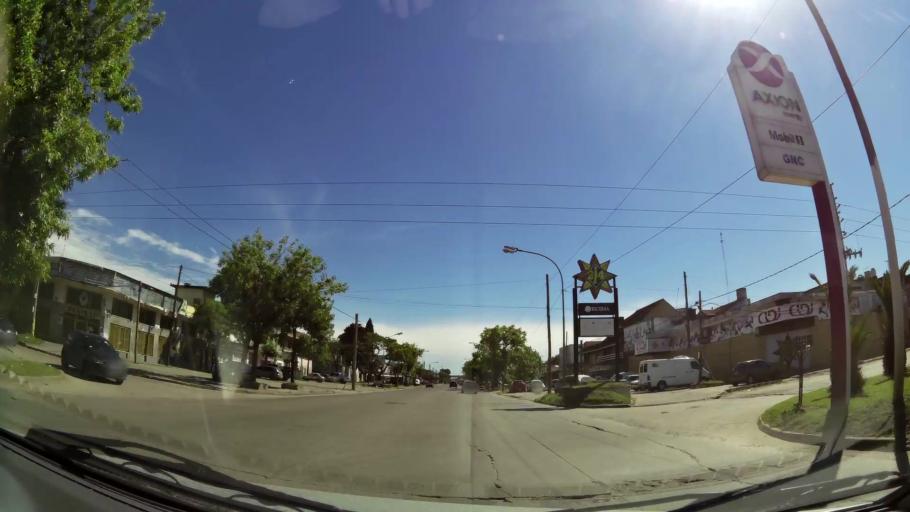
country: AR
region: Buenos Aires
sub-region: Partido de Almirante Brown
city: Adrogue
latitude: -34.7600
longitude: -58.3586
